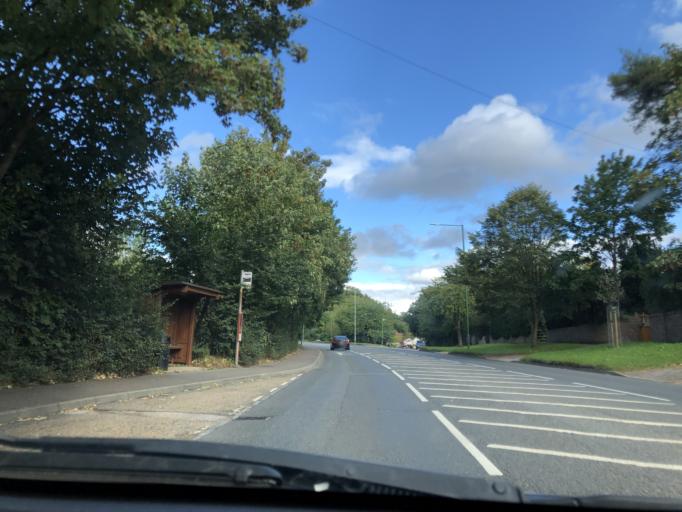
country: GB
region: England
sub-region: Kent
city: Sevenoaks
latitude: 51.2860
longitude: 0.1819
